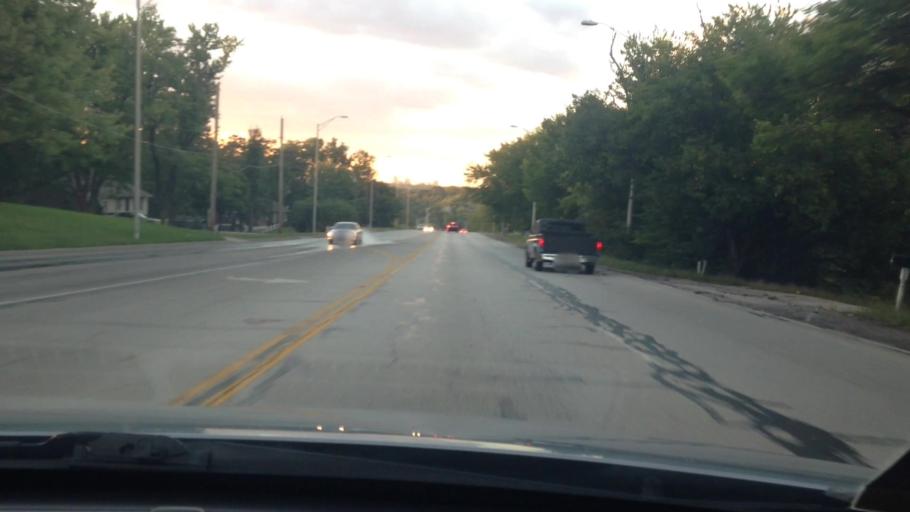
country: US
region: Missouri
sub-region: Jackson County
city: Raytown
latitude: 39.0251
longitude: -94.5047
